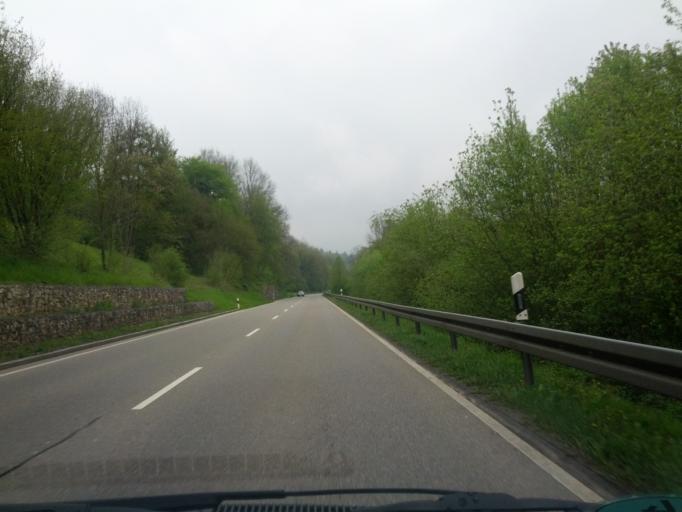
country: DE
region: Baden-Wuerttemberg
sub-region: Freiburg Region
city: Wehr
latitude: 47.6291
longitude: 7.8967
